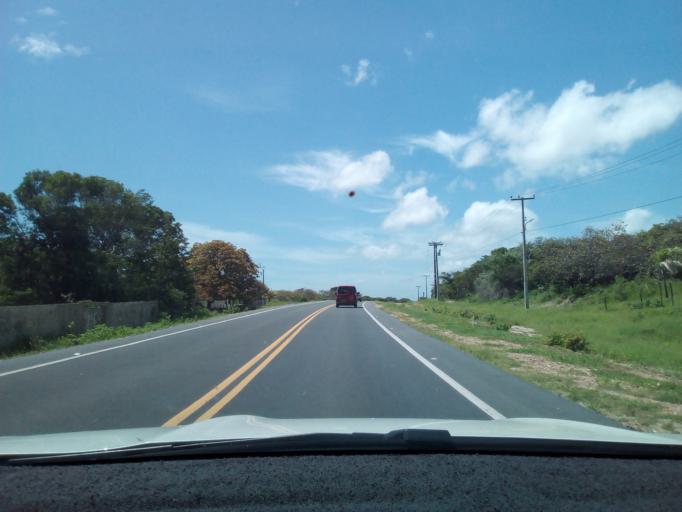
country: BR
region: Ceara
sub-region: Beberibe
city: Beberibe
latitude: -4.2790
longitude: -38.0334
